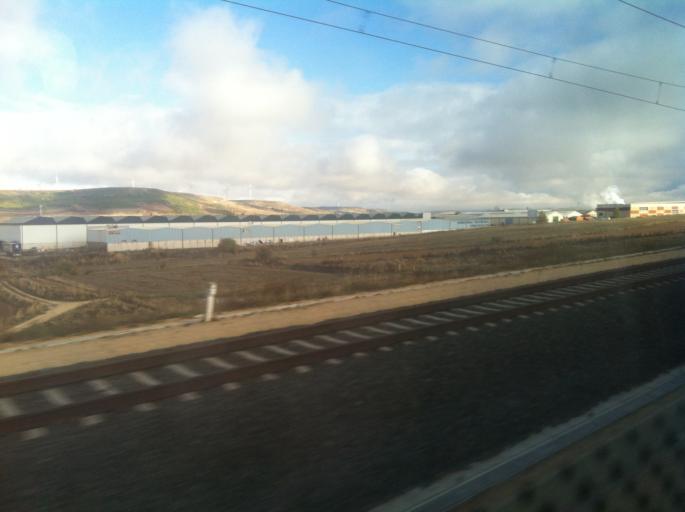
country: ES
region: Castille and Leon
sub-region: Provincia de Burgos
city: Villalbilla de Burgos
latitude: 42.3601
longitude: -3.7533
